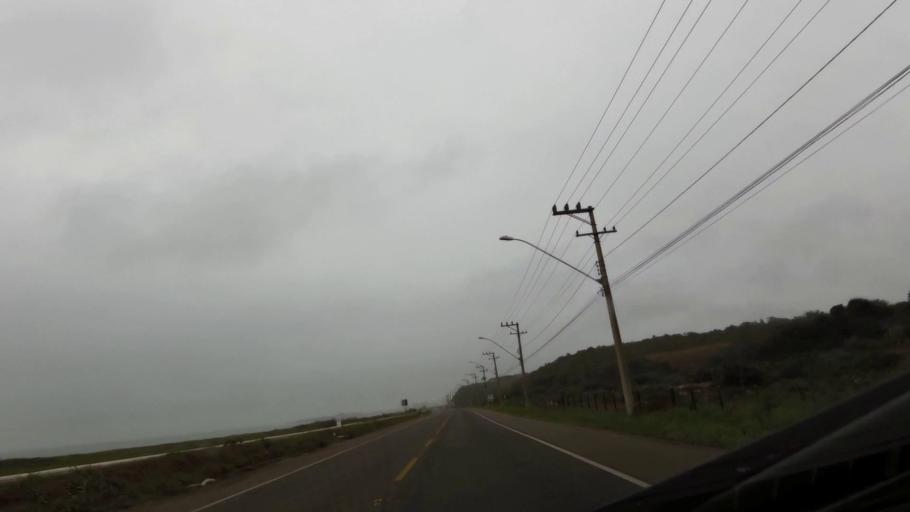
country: BR
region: Espirito Santo
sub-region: Guarapari
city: Guarapari
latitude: -20.7091
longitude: -40.5181
